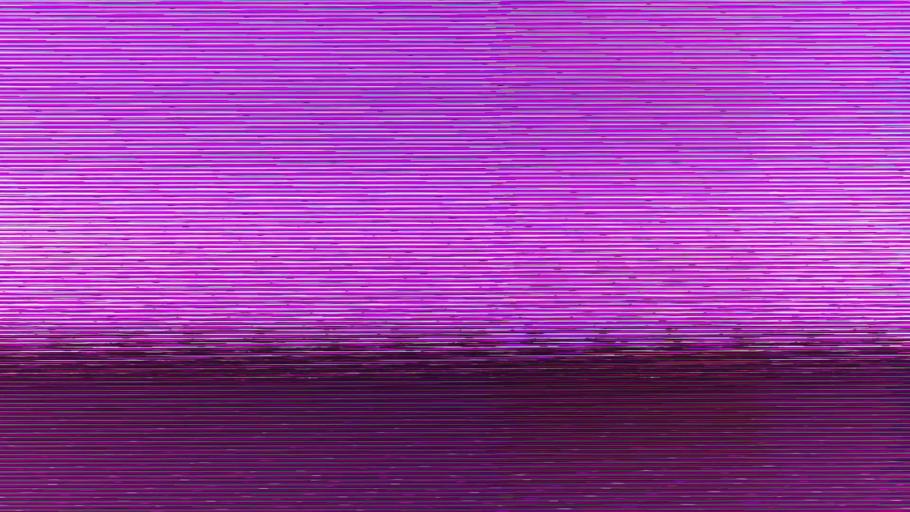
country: US
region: Michigan
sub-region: Oakland County
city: Oxford
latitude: 42.8429
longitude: -83.2754
